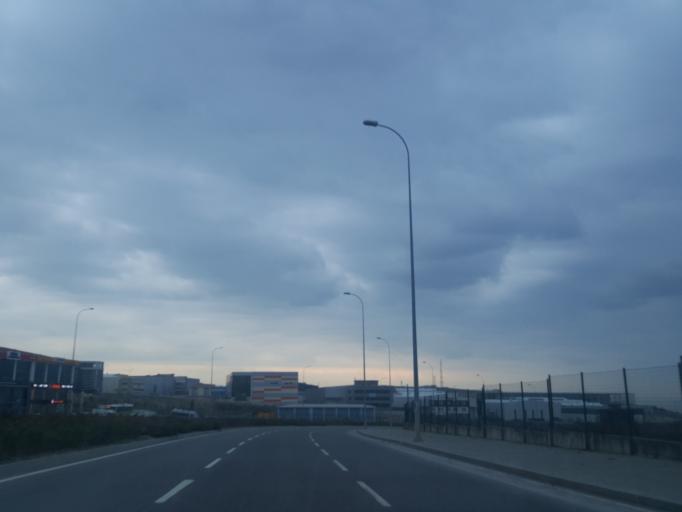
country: TR
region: Kocaeli
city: Tavsancil
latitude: 40.8298
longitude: 29.5694
